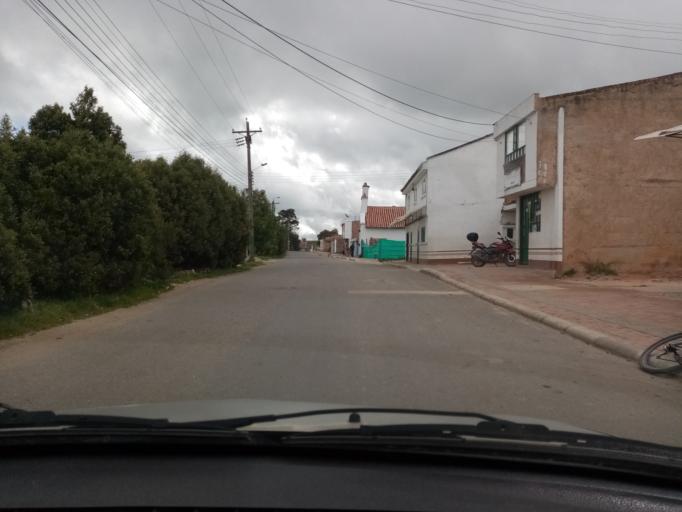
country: CO
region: Boyaca
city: Siachoque
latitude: 5.5584
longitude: -73.2828
